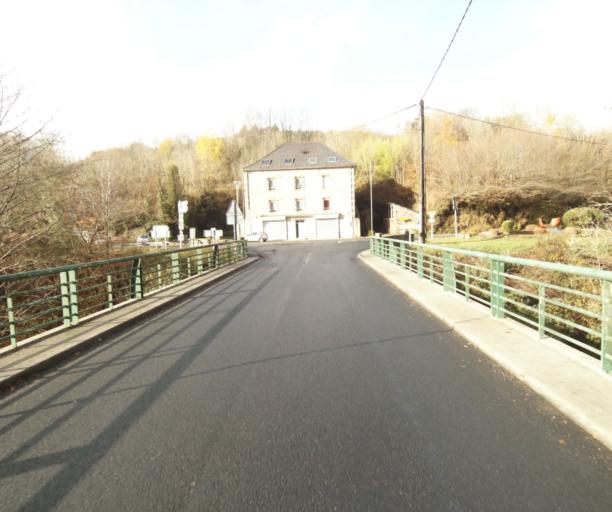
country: FR
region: Limousin
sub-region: Departement de la Correze
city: Cornil
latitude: 45.2165
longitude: 1.7007
